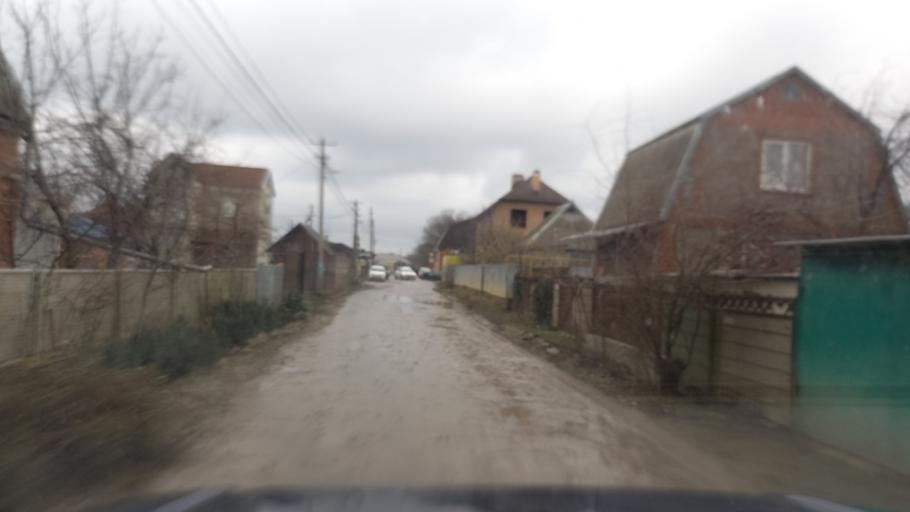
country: RU
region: Krasnodarskiy
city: Pashkovskiy
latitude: 45.0582
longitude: 39.1738
